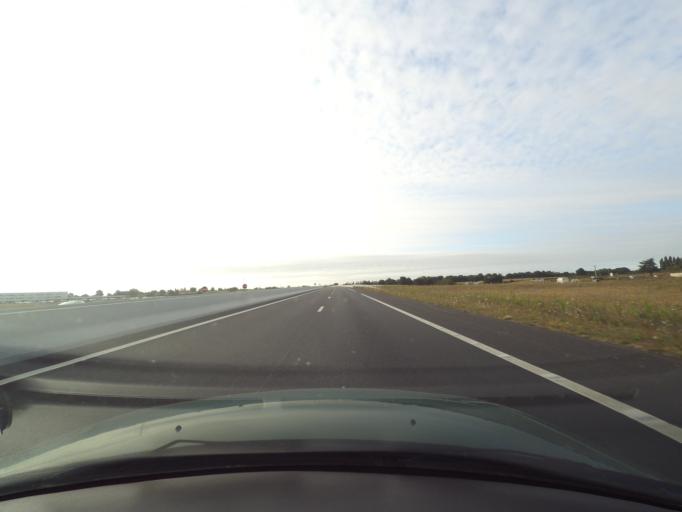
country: FR
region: Pays de la Loire
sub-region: Departement de Maine-et-Loire
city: Cholet
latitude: 47.0384
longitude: -0.9066
